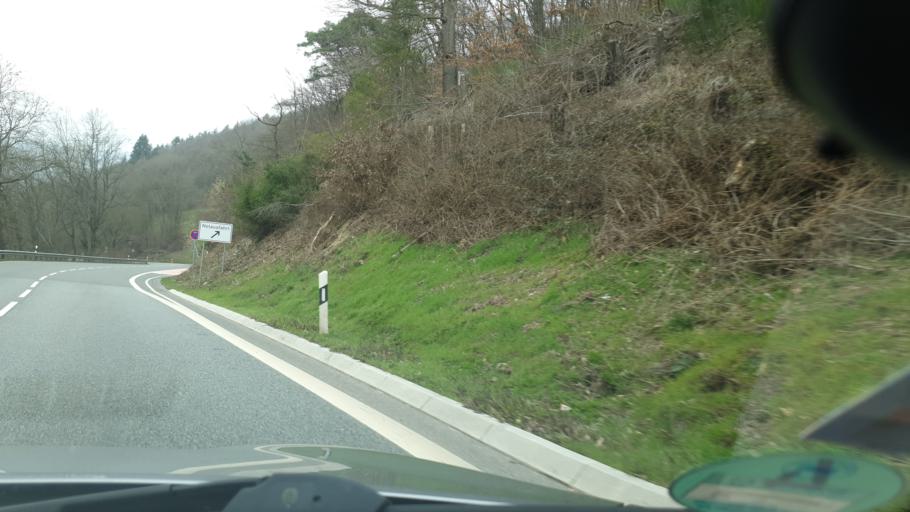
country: DE
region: Rheinland-Pfalz
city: Nassau
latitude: 50.3014
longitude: 7.8016
